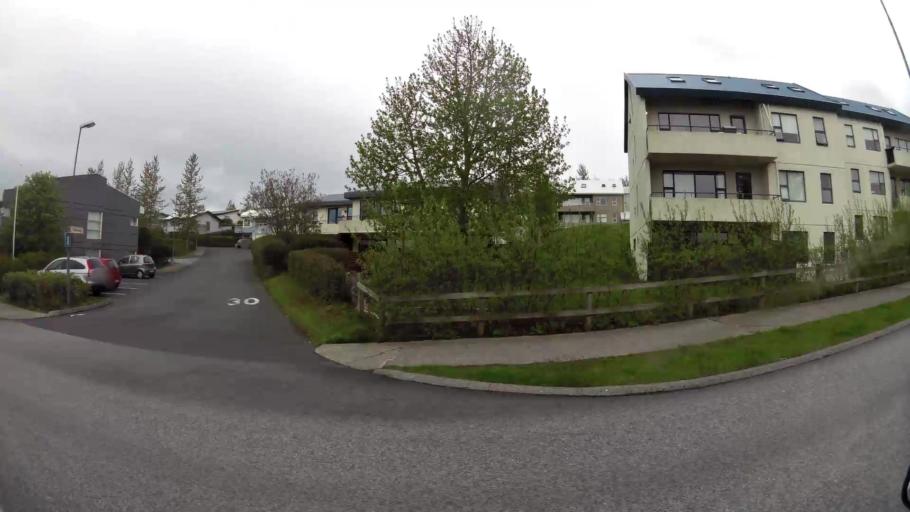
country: IS
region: Capital Region
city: Hafnarfjoerdur
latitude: 64.0650
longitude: -21.9294
